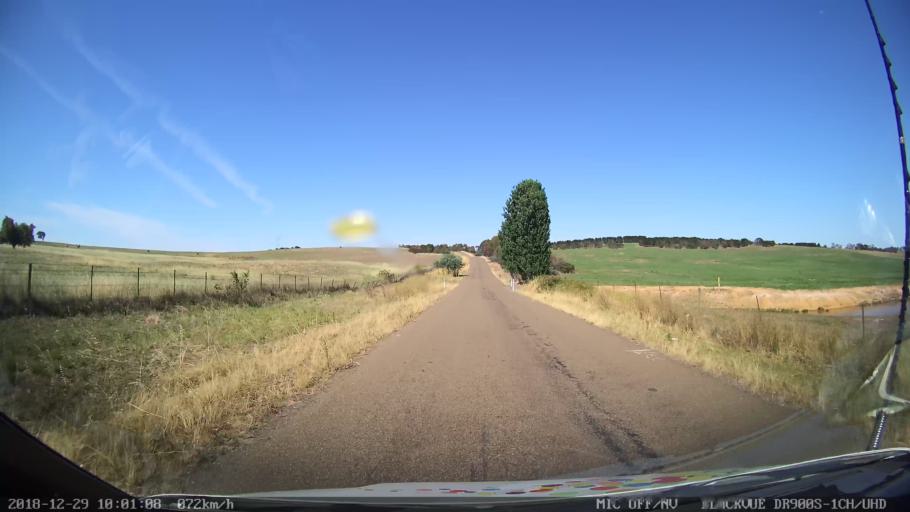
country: AU
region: New South Wales
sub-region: Goulburn Mulwaree
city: Goulburn
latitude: -34.7972
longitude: 149.4801
